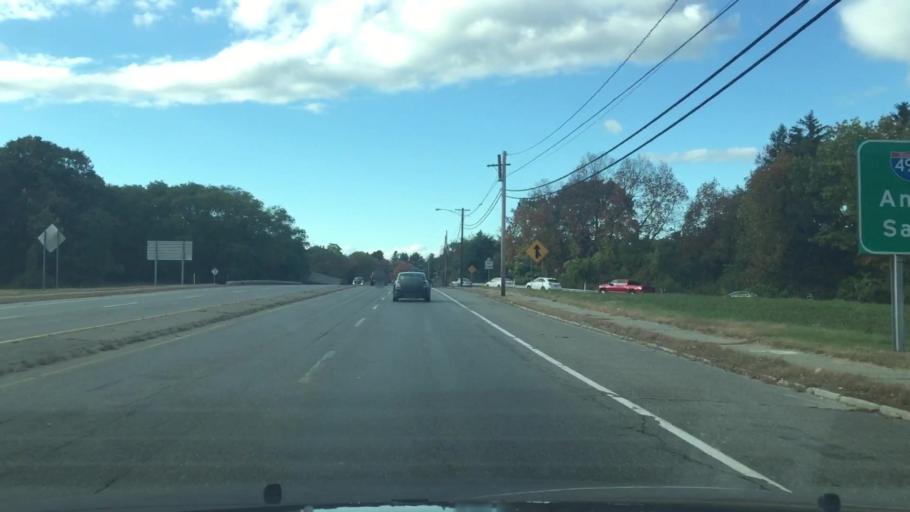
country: US
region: Massachusetts
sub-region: Essex County
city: Haverhill
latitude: 42.7977
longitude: -71.0893
